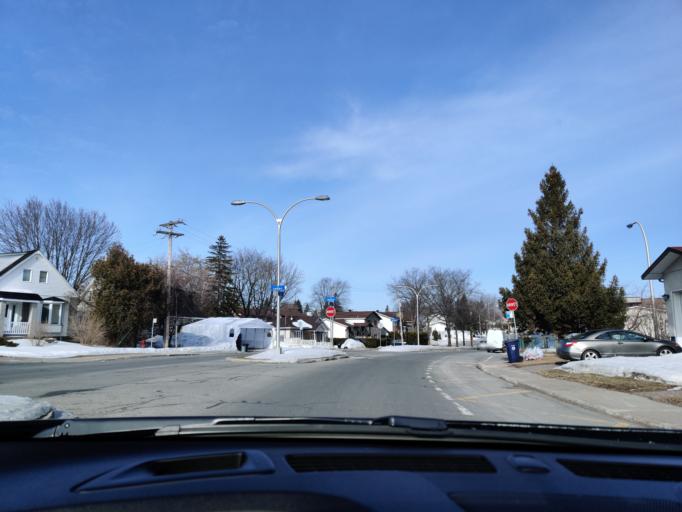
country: CA
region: Quebec
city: Dollard-Des Ormeaux
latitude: 45.5242
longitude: -73.7593
